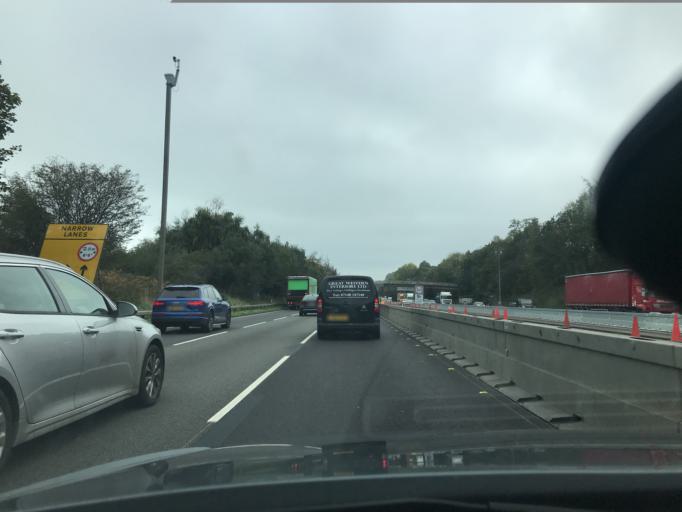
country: GB
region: England
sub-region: Staffordshire
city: Newcastle under Lyme
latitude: 52.9588
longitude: -2.2198
